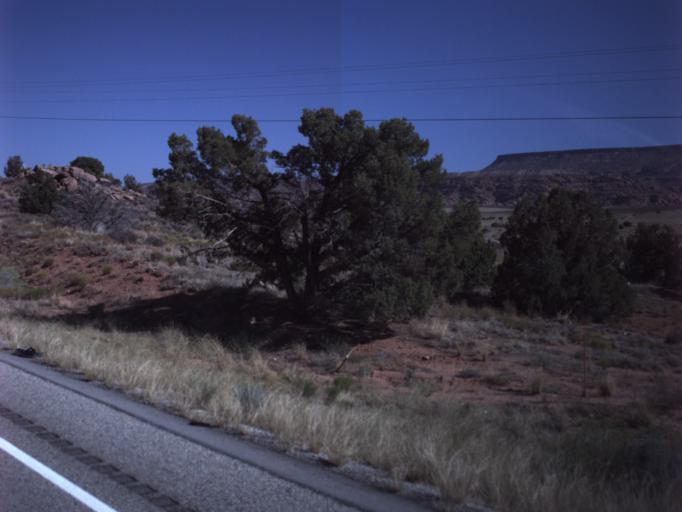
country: US
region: Utah
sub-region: Grand County
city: Moab
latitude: 38.4544
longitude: -109.4401
